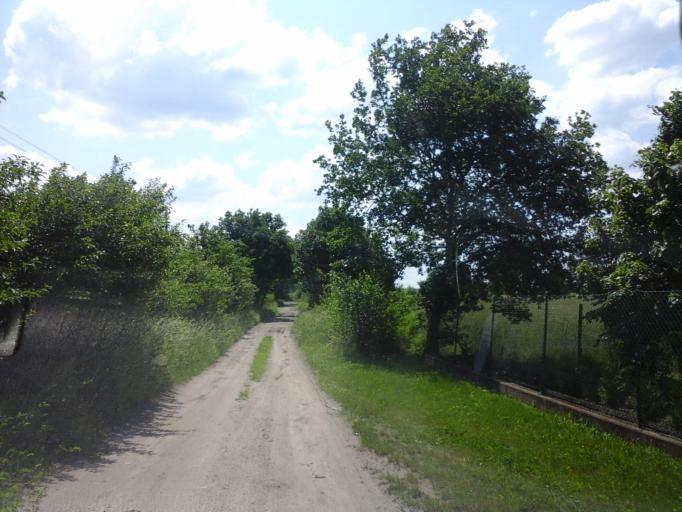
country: PL
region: West Pomeranian Voivodeship
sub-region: Powiat choszczenski
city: Bierzwnik
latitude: 53.0579
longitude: 15.6968
